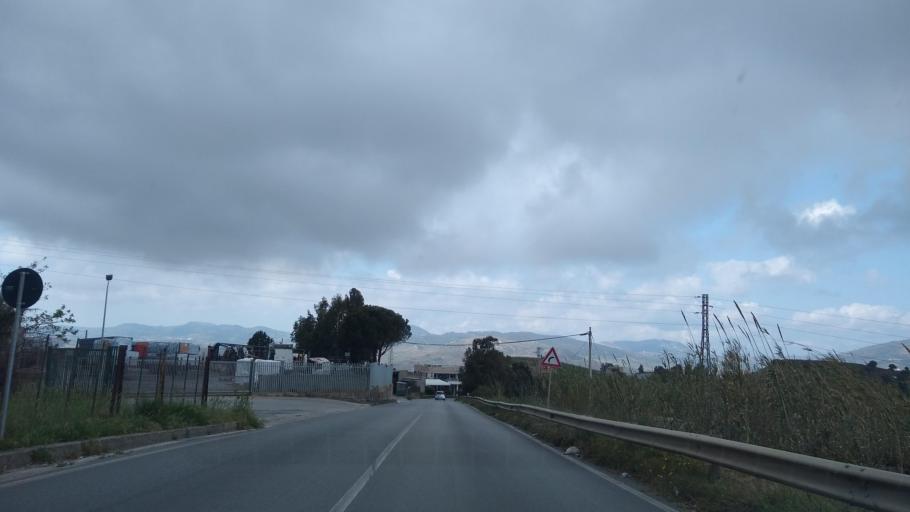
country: IT
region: Sicily
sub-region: Trapani
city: Alcamo
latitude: 37.9774
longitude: 12.9443
